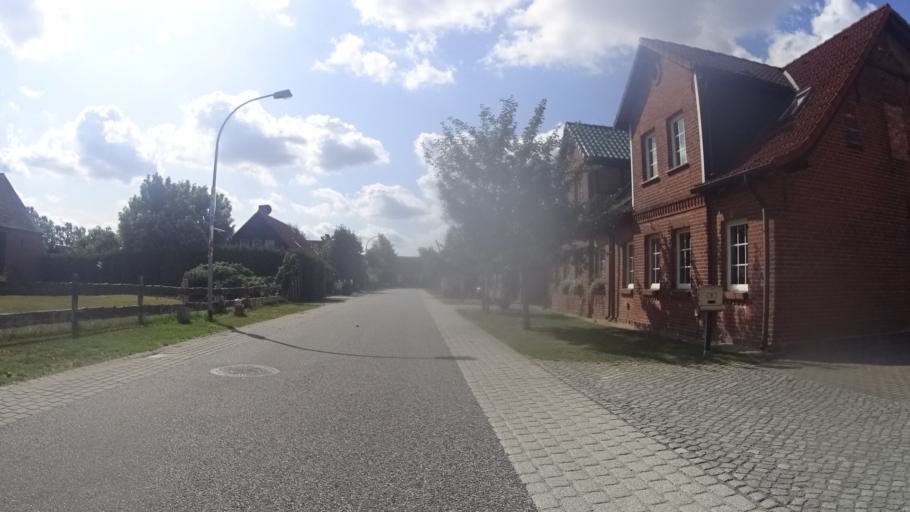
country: DE
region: Brandenburg
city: Ruhstadt
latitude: 52.9220
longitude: 11.8706
